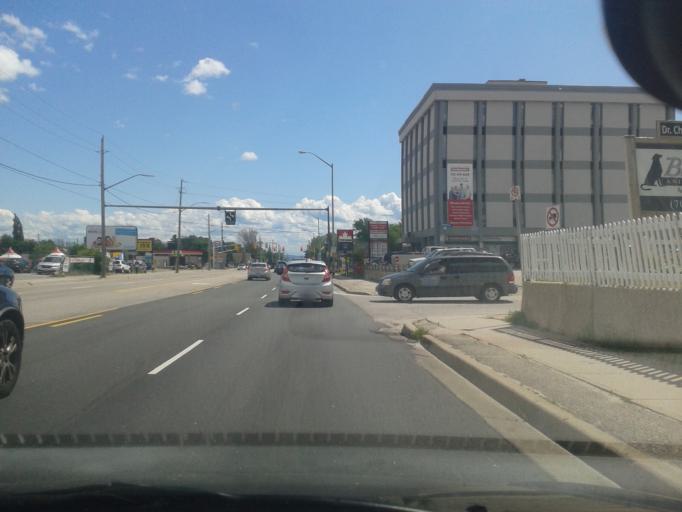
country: CA
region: Ontario
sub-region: Nipissing District
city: North Bay
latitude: 46.3273
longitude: -79.4663
